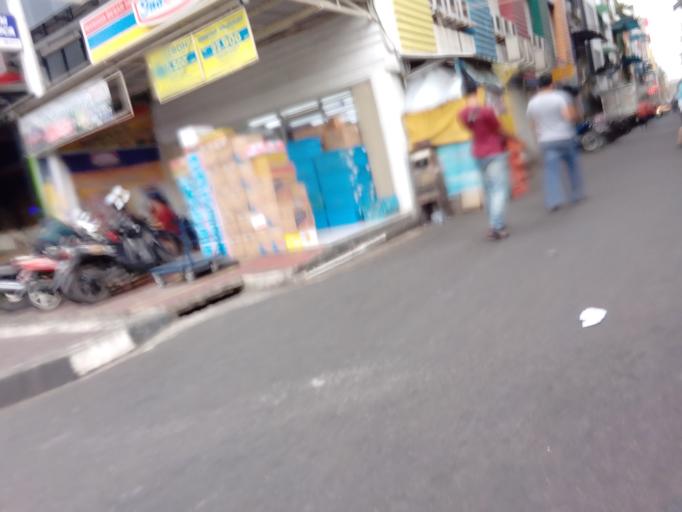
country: ID
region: Jakarta Raya
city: Jakarta
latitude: -6.1496
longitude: 106.8211
